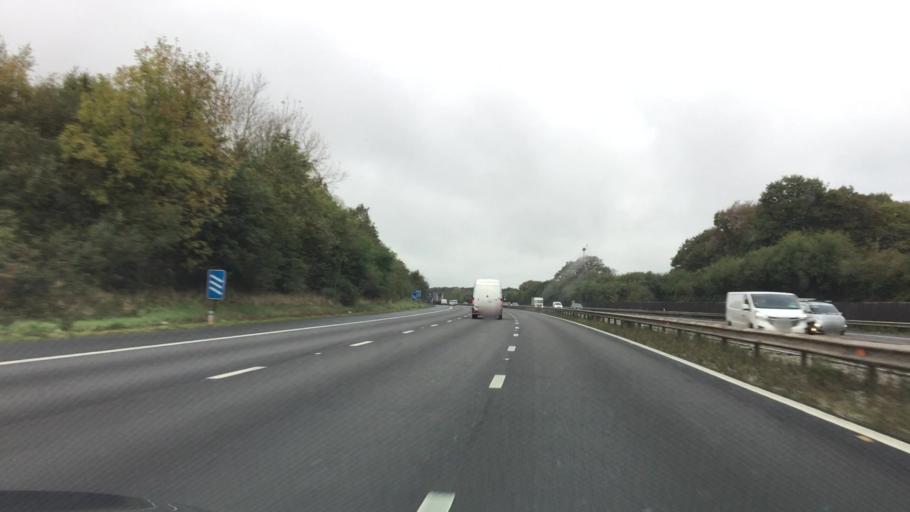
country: GB
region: England
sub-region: Solihull
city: Tidbury Green
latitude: 52.3539
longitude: -1.8740
